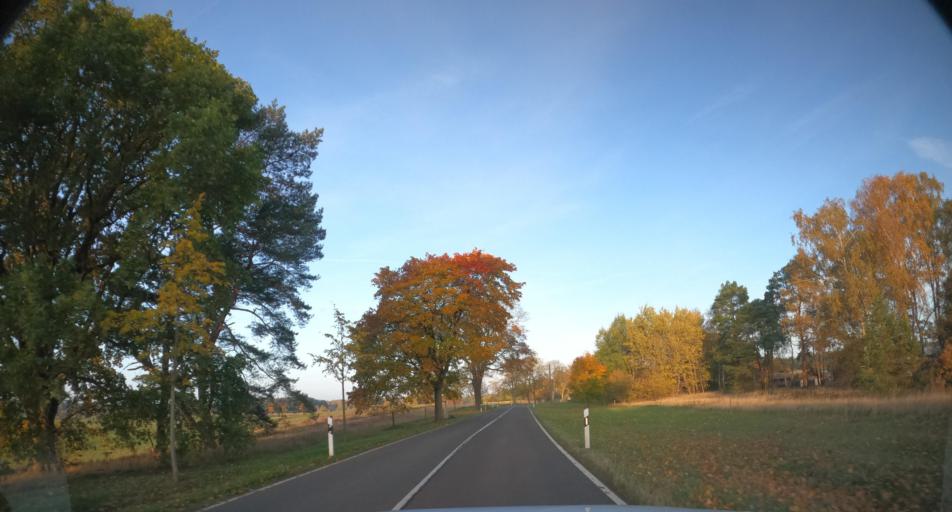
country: DE
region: Mecklenburg-Vorpommern
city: Ahlbeck
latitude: 53.6250
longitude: 14.2729
